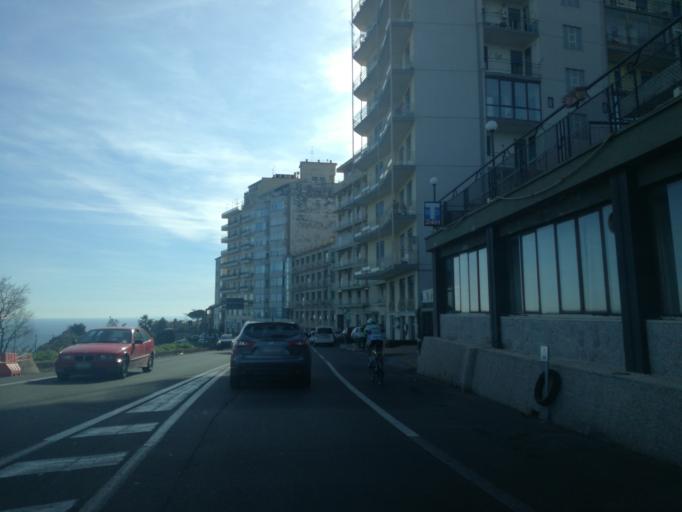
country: IT
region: Sicily
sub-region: Catania
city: Acireale
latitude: 37.6184
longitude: 15.1697
